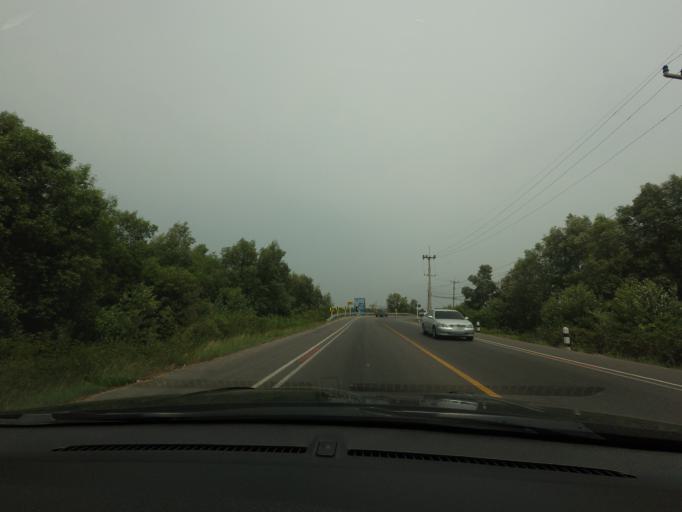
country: TH
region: Phetchaburi
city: Ban Laem
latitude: 13.2848
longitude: 99.9247
